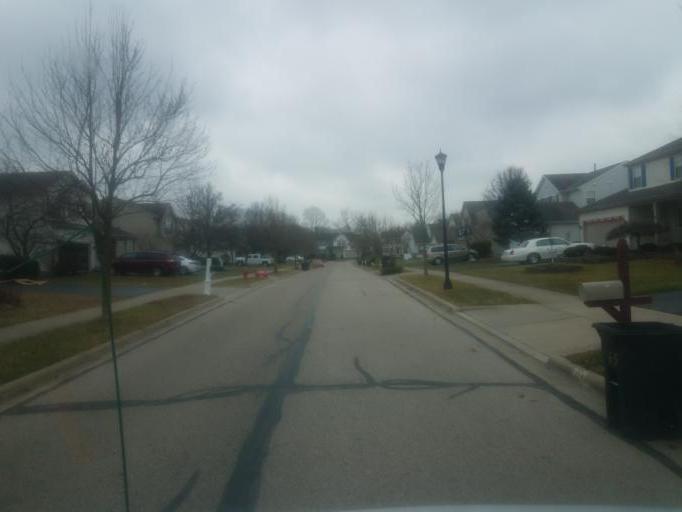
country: US
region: Ohio
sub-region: Franklin County
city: Westerville
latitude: 40.1362
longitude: -82.9596
